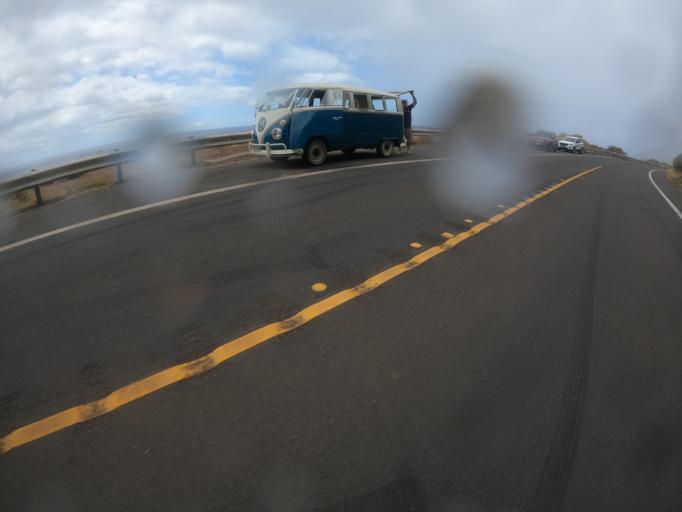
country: US
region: Hawaii
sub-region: Honolulu County
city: Makaha Valley
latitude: 21.5416
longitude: -158.2360
